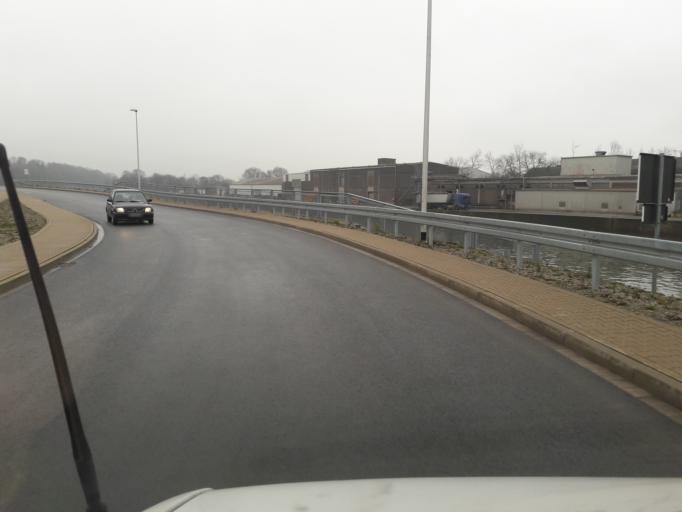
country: DE
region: North Rhine-Westphalia
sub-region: Regierungsbezirk Detmold
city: Minden
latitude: 52.3062
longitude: 8.9223
